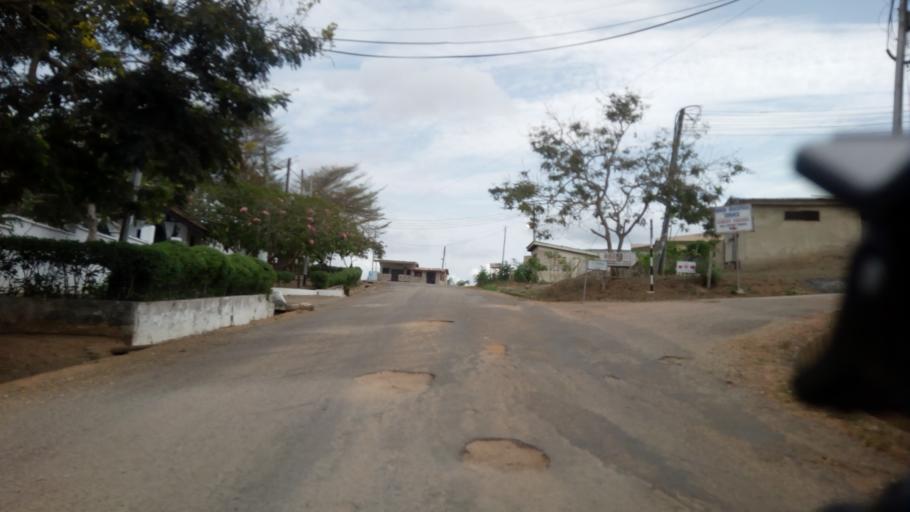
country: GH
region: Central
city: Cape Coast
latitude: 5.1039
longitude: -1.2713
